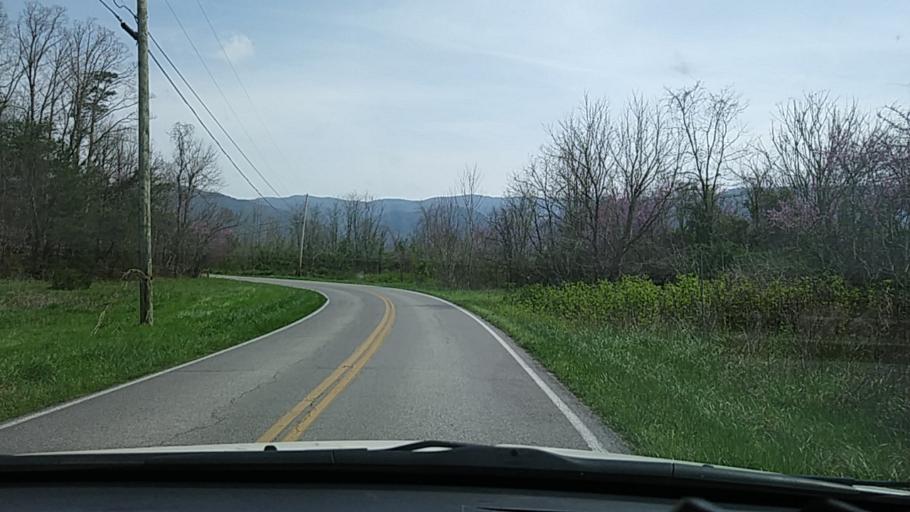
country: US
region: Tennessee
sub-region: Greene County
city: Tusculum
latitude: 36.0962
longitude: -82.7375
